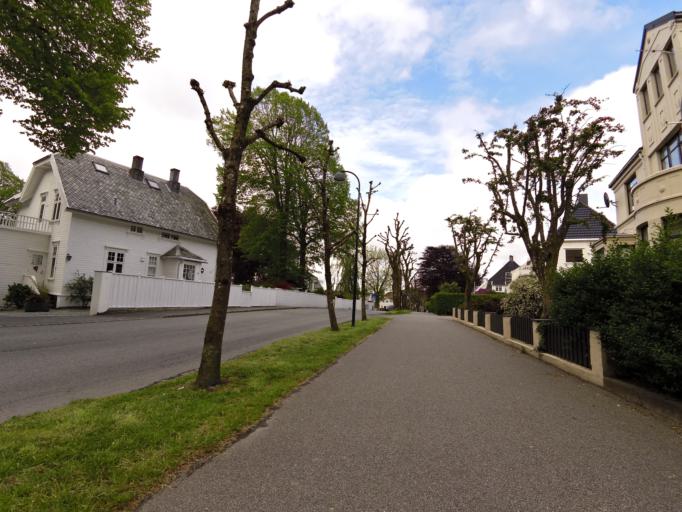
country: NO
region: Rogaland
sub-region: Stavanger
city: Stavanger
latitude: 58.9652
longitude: 5.7192
